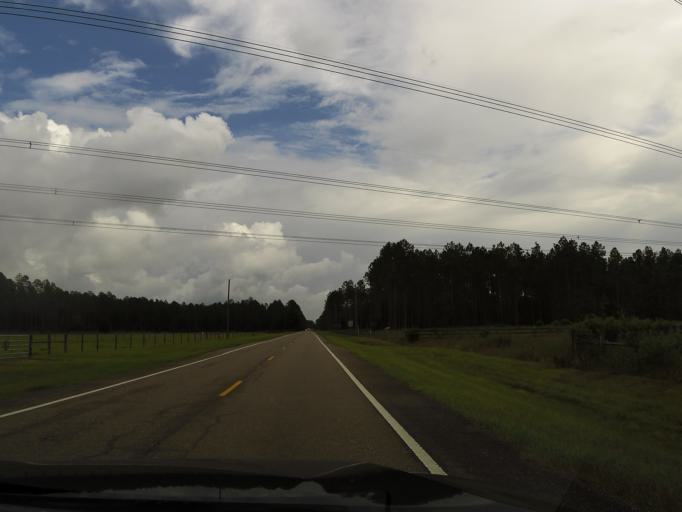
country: US
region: Florida
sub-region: Duval County
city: Baldwin
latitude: 30.3738
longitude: -81.9352
